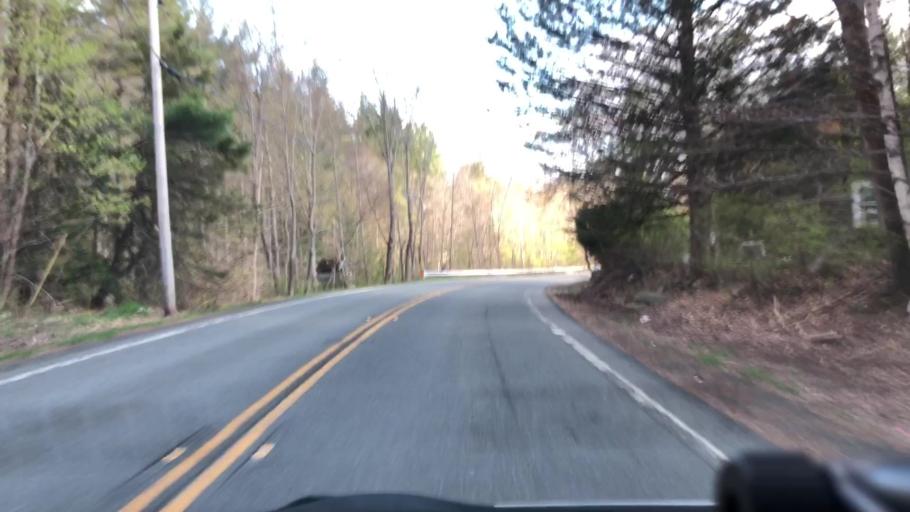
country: US
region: Massachusetts
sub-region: Hampshire County
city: Chesterfield
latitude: 42.3559
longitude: -72.9055
